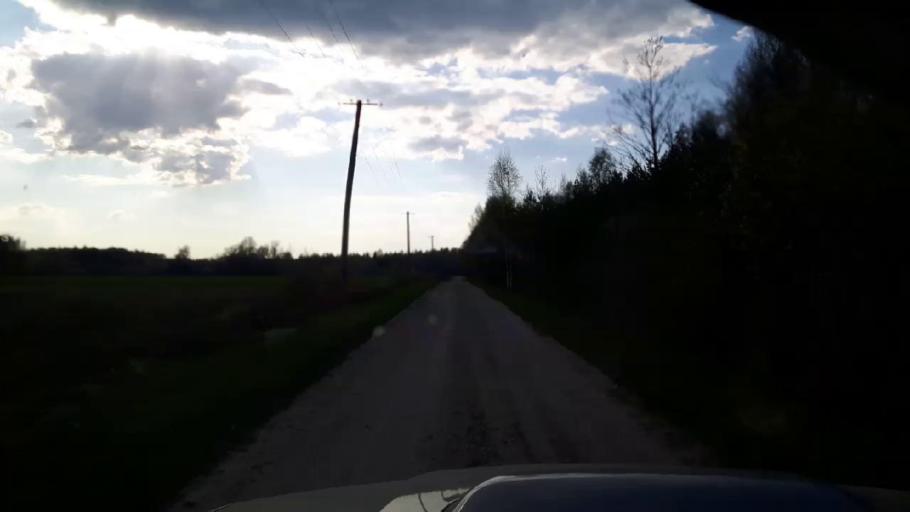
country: EE
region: Paernumaa
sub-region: Tootsi vald
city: Tootsi
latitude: 58.4703
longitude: 24.9089
